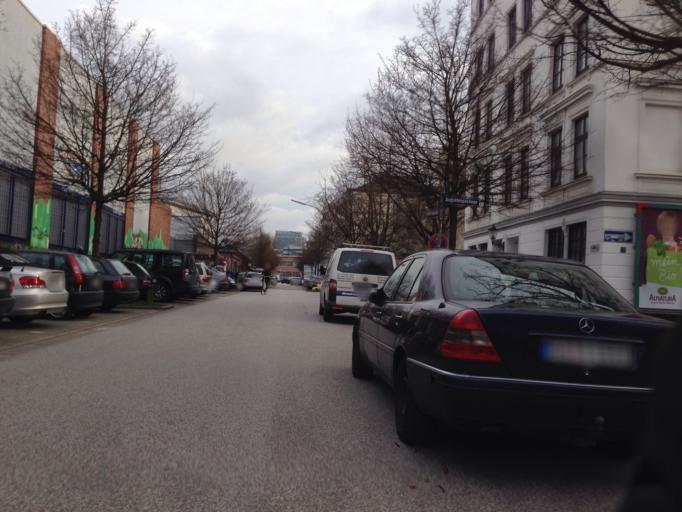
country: DE
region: Hamburg
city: St. Pauli
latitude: 53.5592
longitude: 9.9669
